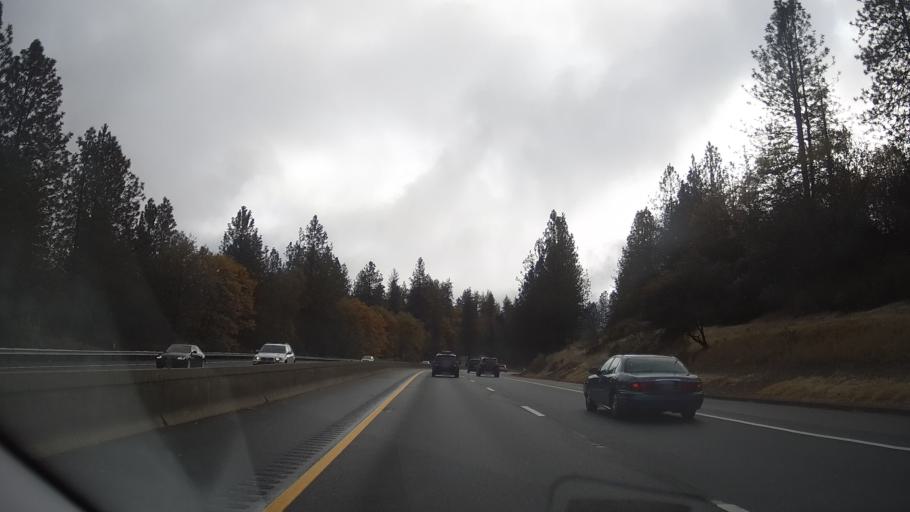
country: US
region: California
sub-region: Placer County
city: Meadow Vista
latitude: 39.0113
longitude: -120.9898
